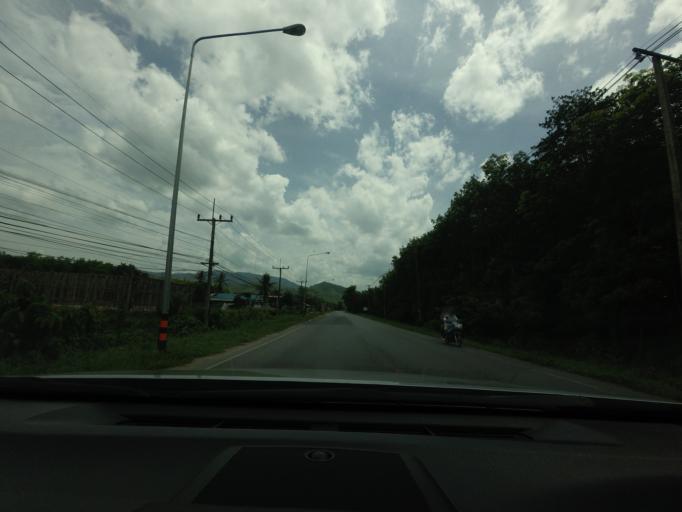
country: TH
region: Yala
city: Raman
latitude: 6.4571
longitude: 101.3614
